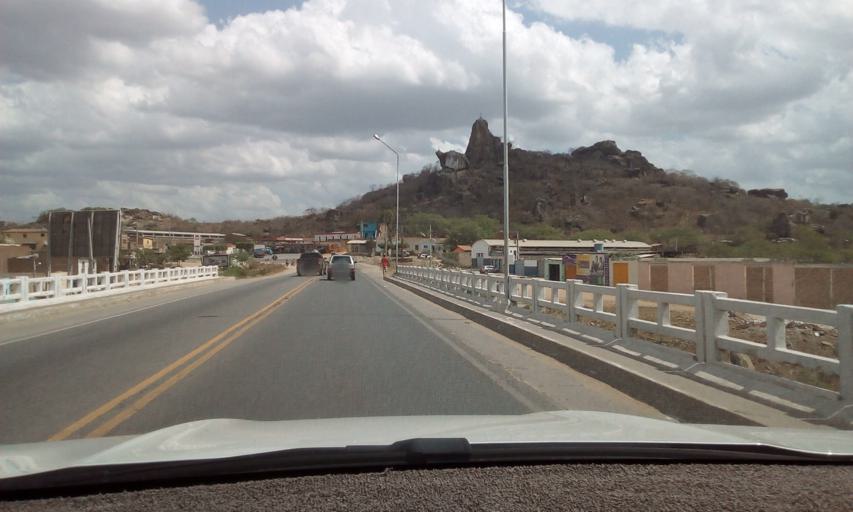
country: BR
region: Pernambuco
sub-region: Toritama
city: Toritama
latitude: -8.0119
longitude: -36.0573
